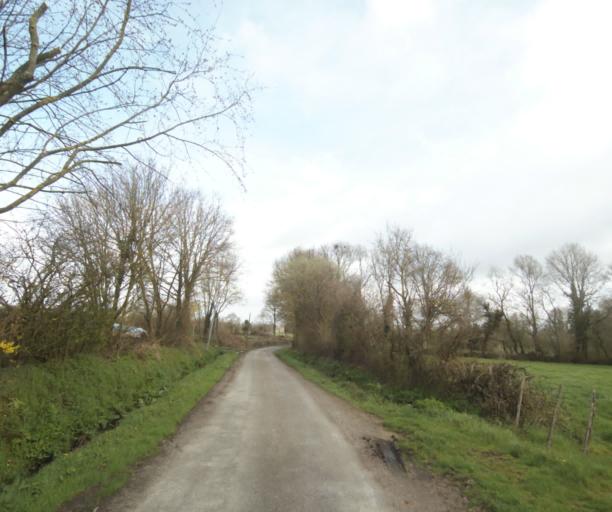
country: FR
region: Pays de la Loire
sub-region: Departement de la Loire-Atlantique
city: Bouvron
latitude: 47.4158
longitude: -1.8747
